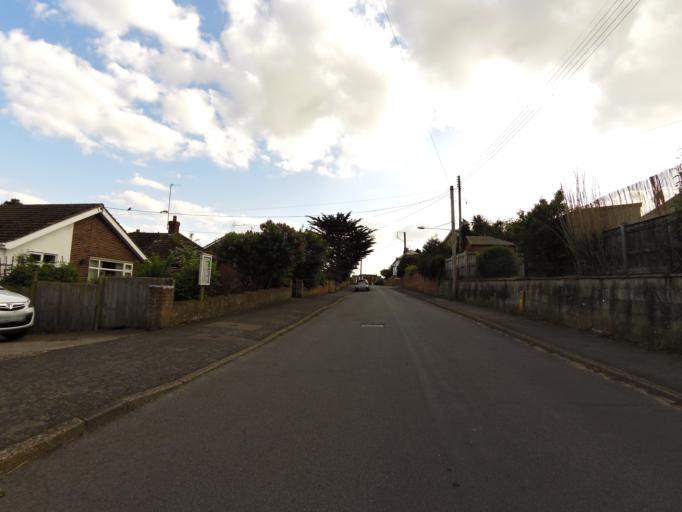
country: GB
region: England
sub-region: Suffolk
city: Beccles
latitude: 52.4470
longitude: 1.5669
